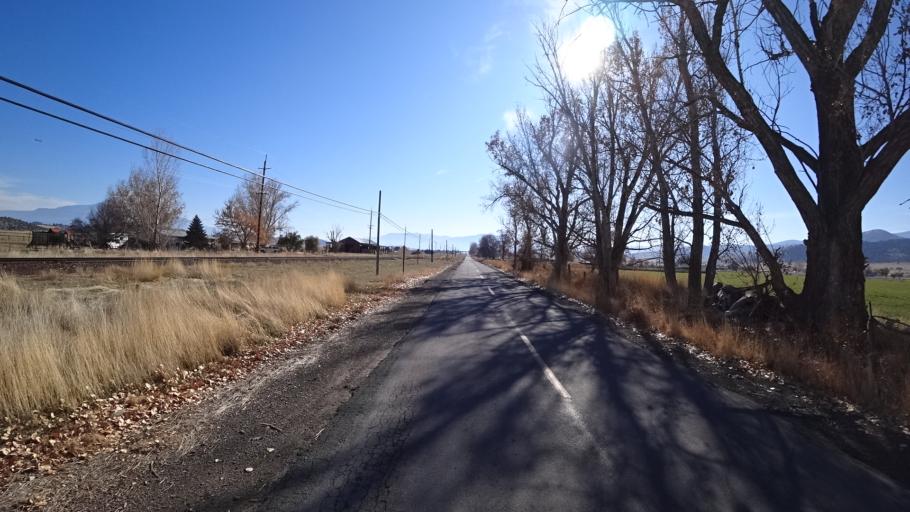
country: US
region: California
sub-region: Siskiyou County
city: Montague
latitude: 41.6371
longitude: -122.5216
